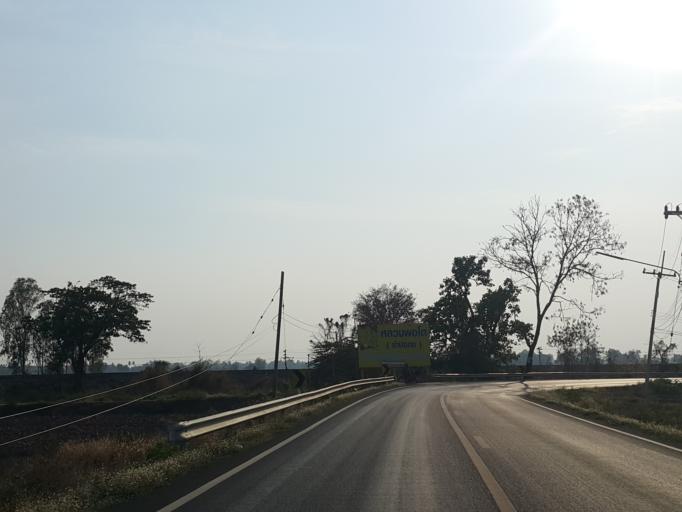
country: TH
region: Phitsanulok
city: Phrom Phiram
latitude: 17.1497
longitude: 100.1267
